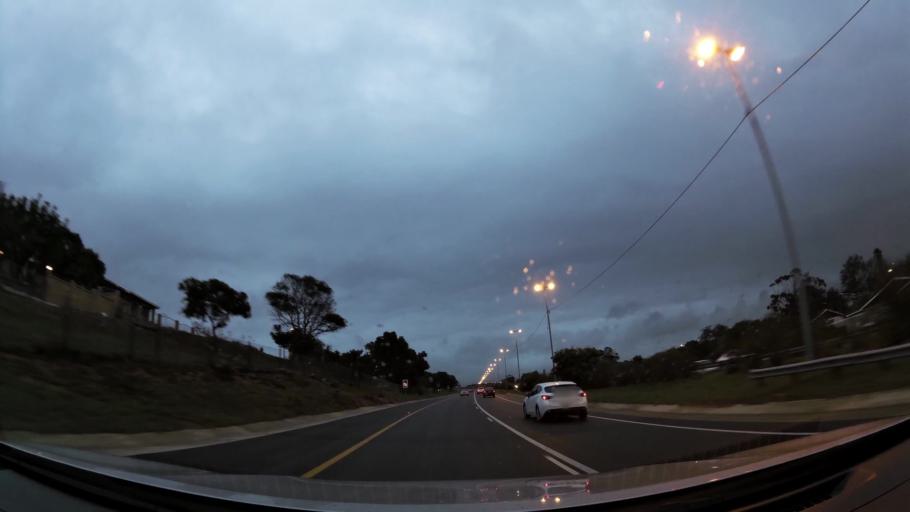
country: ZA
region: Eastern Cape
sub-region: Nelson Mandela Bay Metropolitan Municipality
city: Port Elizabeth
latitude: -33.9364
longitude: 25.5557
